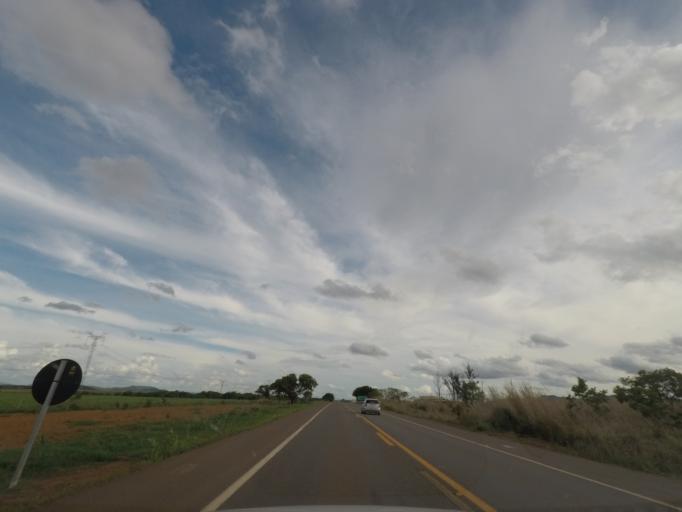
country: BR
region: Goias
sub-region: Padre Bernardo
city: Padre Bernardo
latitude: -15.4415
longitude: -48.6185
